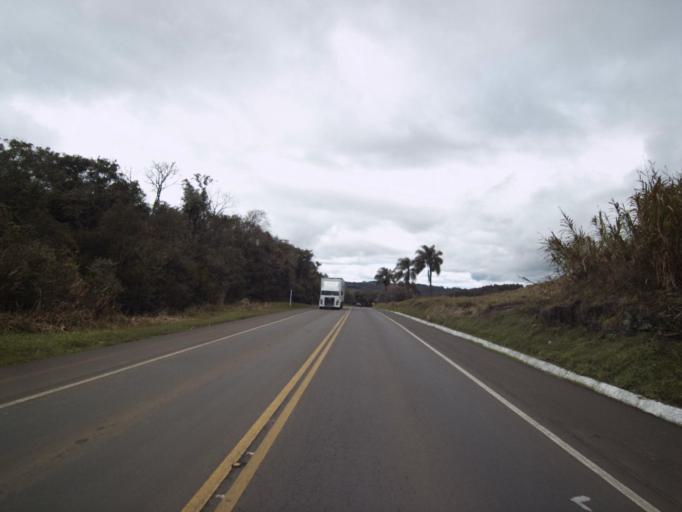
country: BR
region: Santa Catarina
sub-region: Concordia
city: Concordia
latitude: -27.2650
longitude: -51.9597
